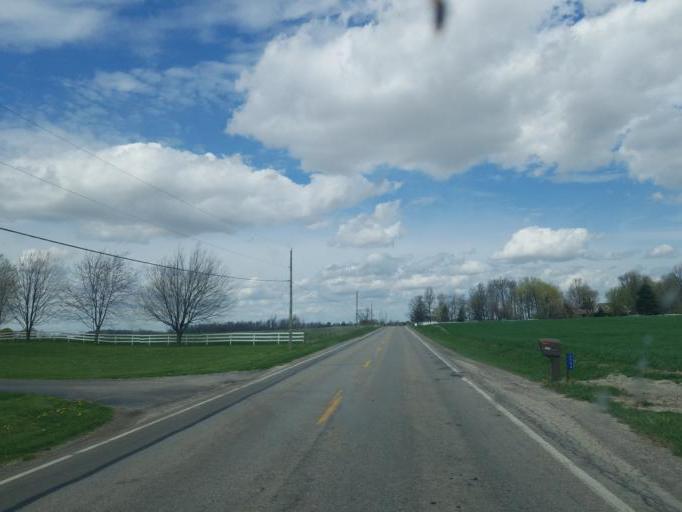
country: US
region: Ohio
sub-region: Crawford County
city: Bucyrus
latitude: 40.8450
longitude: -82.9900
